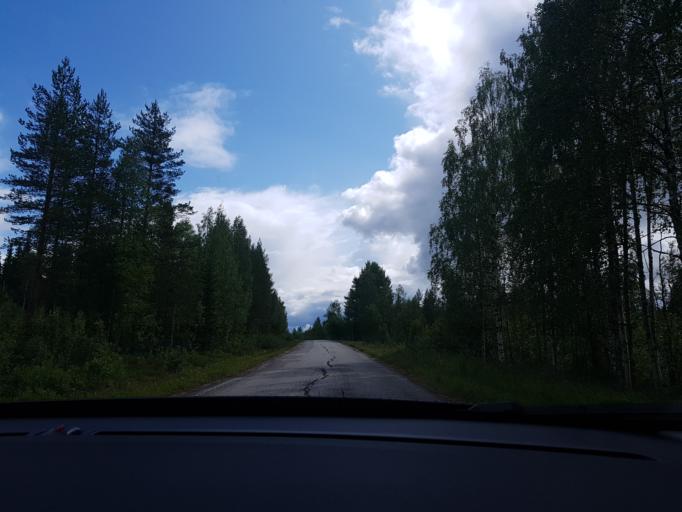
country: FI
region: Kainuu
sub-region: Kehys-Kainuu
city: Kuhmo
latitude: 64.4522
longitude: 29.6641
